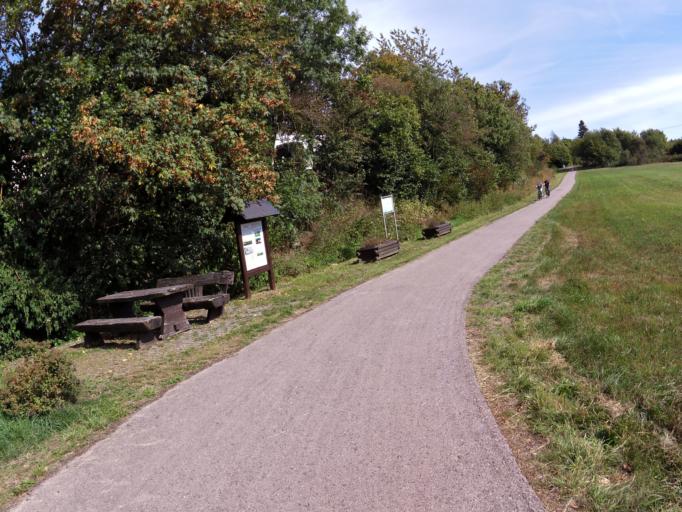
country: DE
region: Rheinland-Pfalz
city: Euscheid
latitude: 50.1274
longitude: 6.2680
